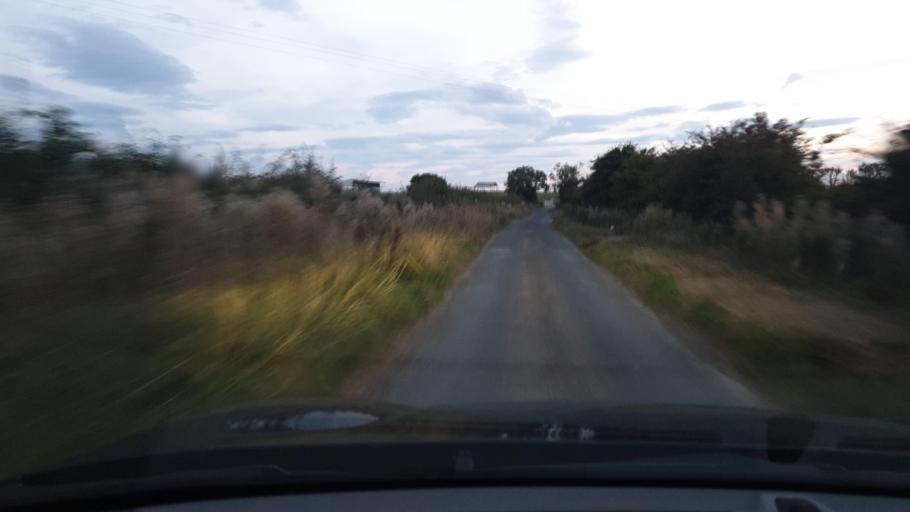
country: IE
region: Leinster
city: An Ros
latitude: 53.5390
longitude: -6.1236
